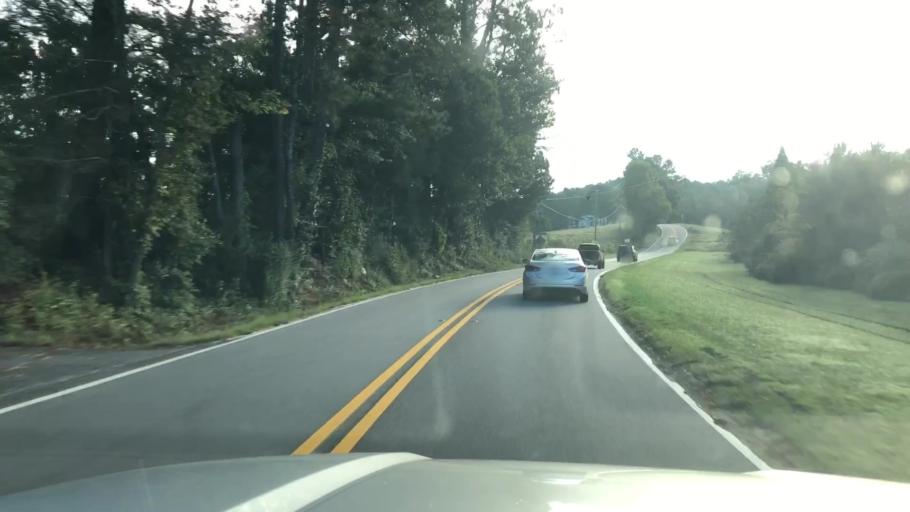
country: US
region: Georgia
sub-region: Bartow County
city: Emerson
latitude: 34.0821
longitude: -84.7414
